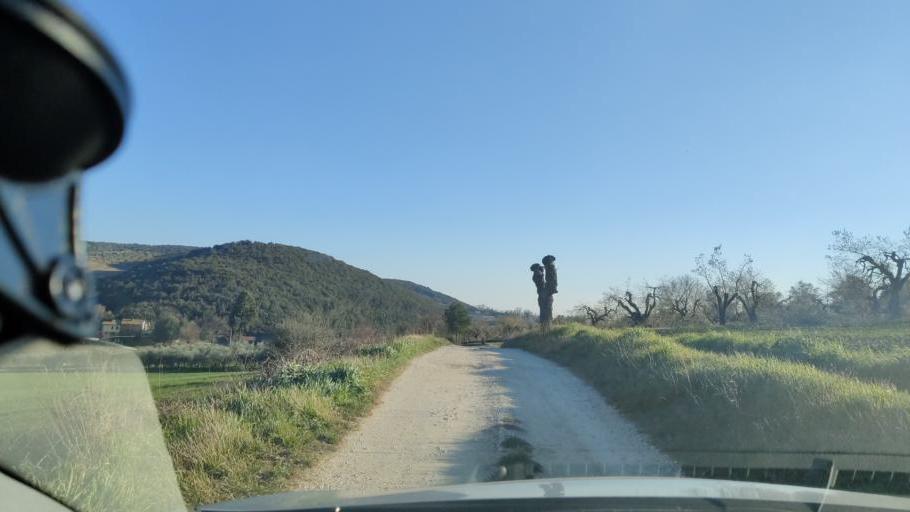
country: IT
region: Umbria
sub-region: Provincia di Terni
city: Fornole
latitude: 42.5602
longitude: 12.4494
